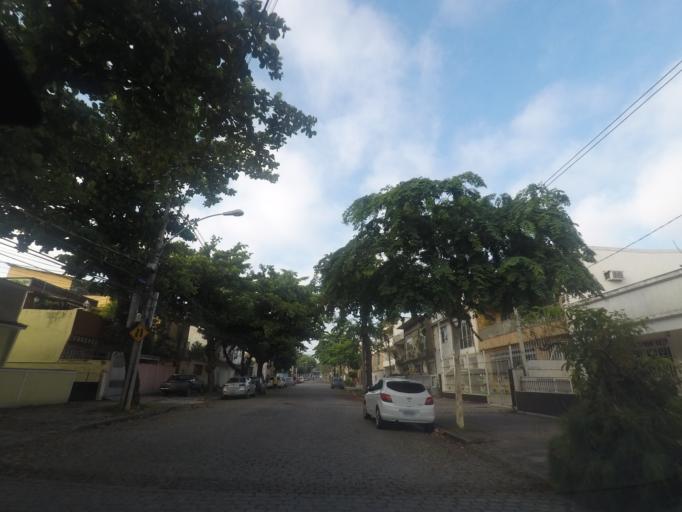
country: BR
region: Rio de Janeiro
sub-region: Duque De Caxias
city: Duque de Caxias
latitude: -22.8386
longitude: -43.2654
